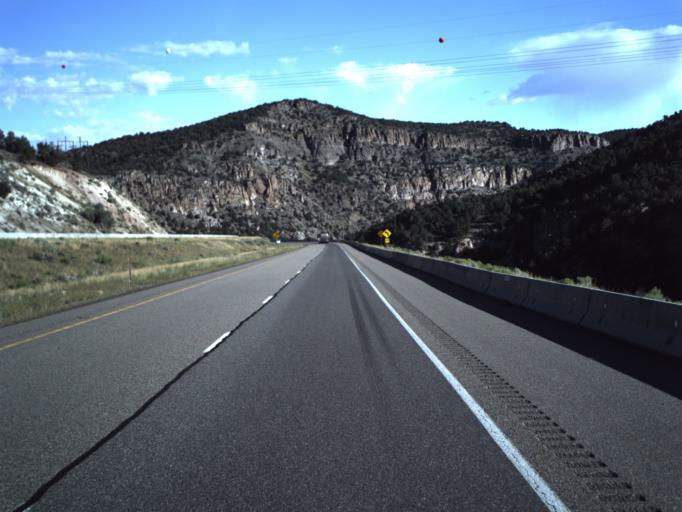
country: US
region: Utah
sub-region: Sevier County
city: Monroe
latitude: 38.5581
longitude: -112.4252
